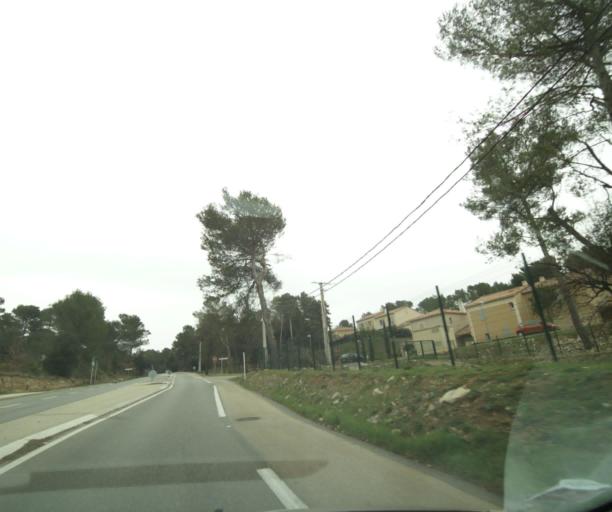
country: FR
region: Provence-Alpes-Cote d'Azur
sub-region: Departement des Bouches-du-Rhone
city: Greasque
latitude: 43.4363
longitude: 5.5590
